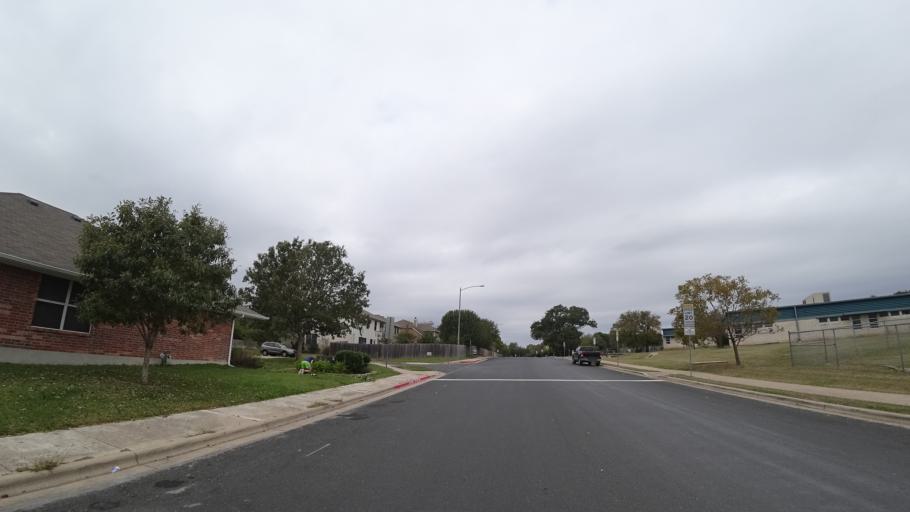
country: US
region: Texas
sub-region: Travis County
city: Shady Hollow
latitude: 30.1524
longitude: -97.8519
